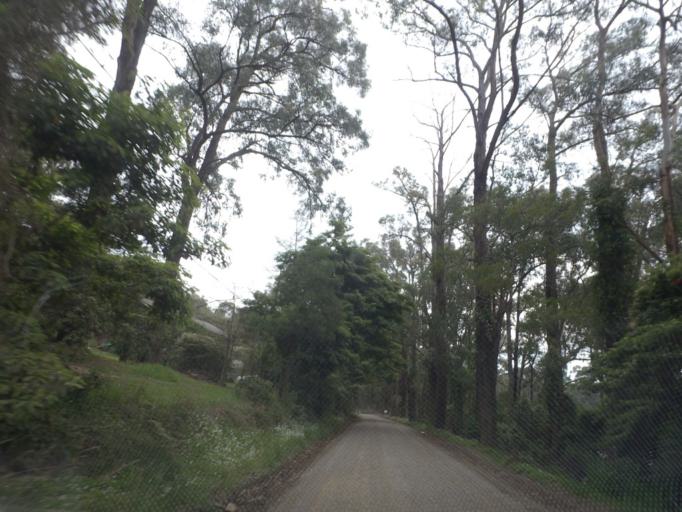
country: AU
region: Victoria
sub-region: Knox
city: The Basin
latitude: -37.8558
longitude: 145.3285
